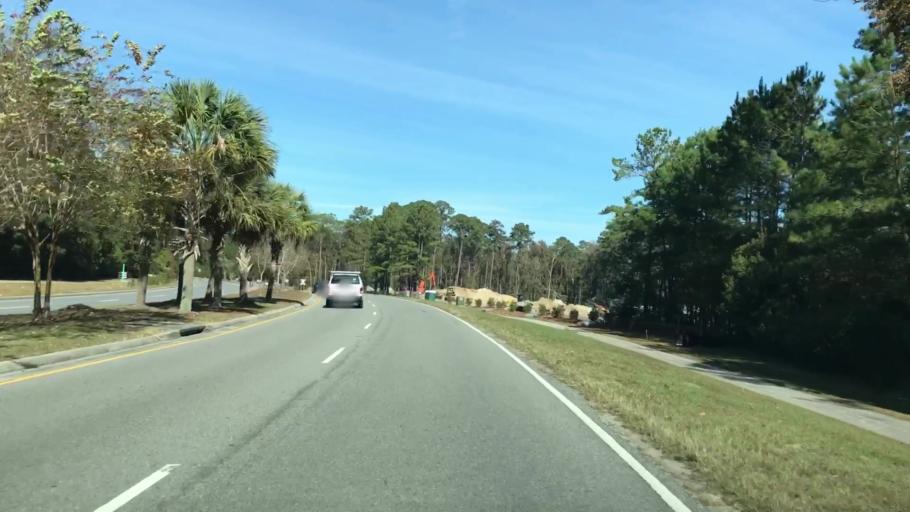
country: US
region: South Carolina
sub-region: Beaufort County
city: Bluffton
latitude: 32.2866
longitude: -80.9090
